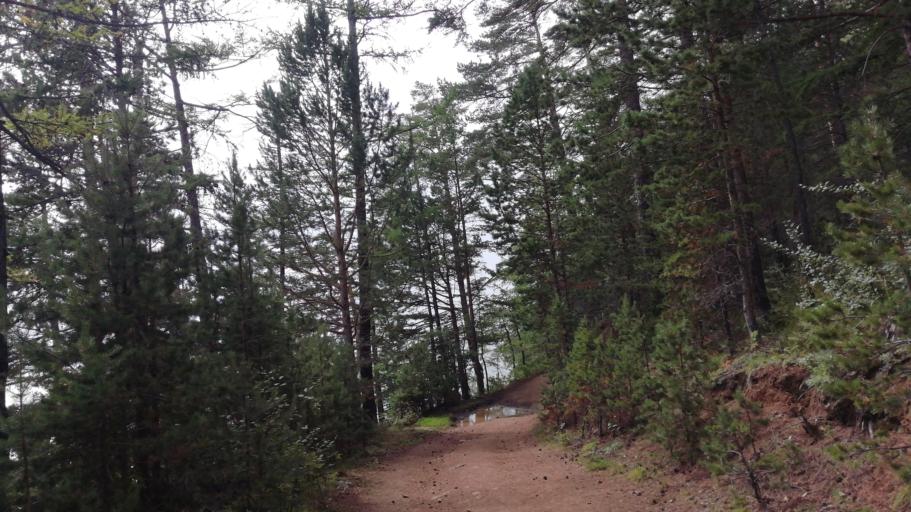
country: RU
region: Irkutsk
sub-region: Irkutskiy Rayon
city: Listvyanka
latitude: 51.8917
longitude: 105.0445
